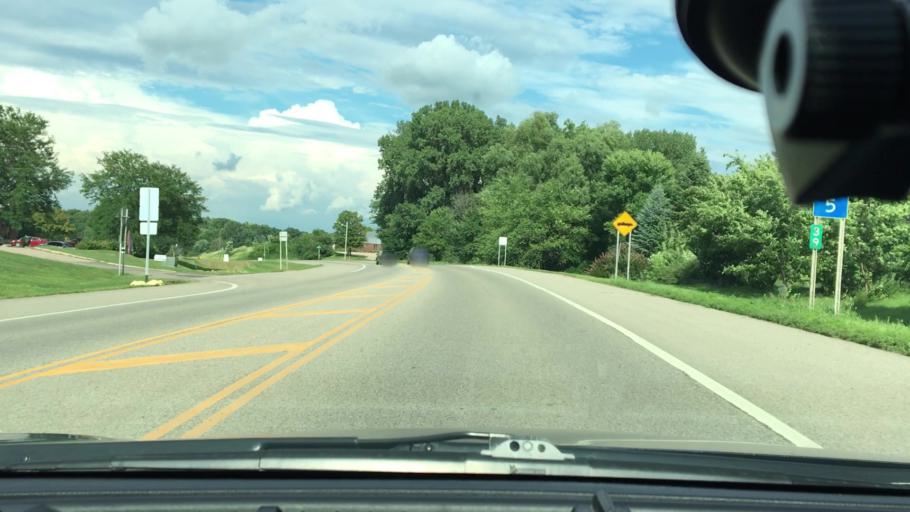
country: US
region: Minnesota
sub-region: Carver County
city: Victoria
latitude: 44.8586
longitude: -93.6596
